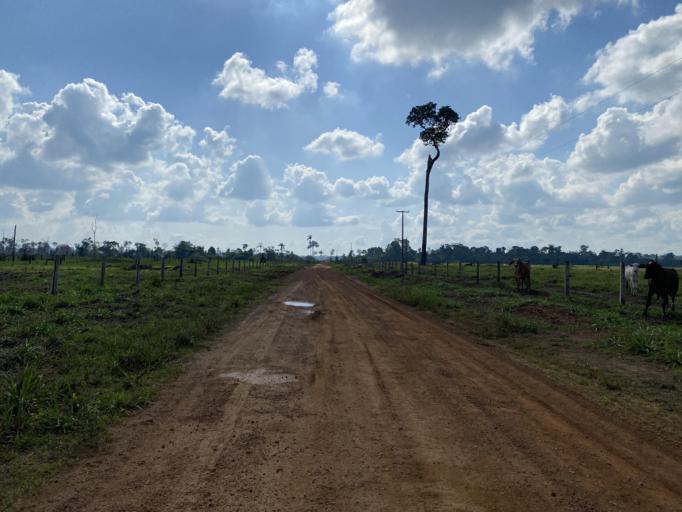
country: BR
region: Rondonia
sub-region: Porto Velho
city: Porto Velho
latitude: -8.5929
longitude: -63.3124
